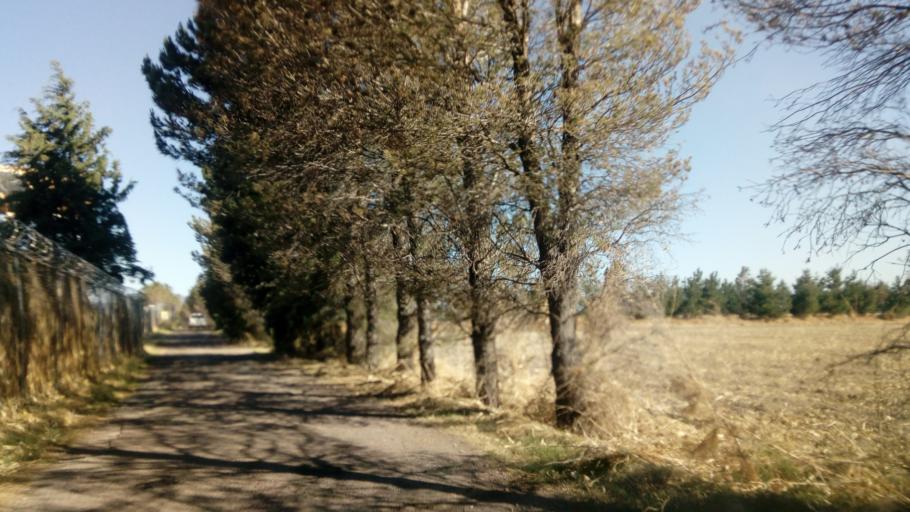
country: MX
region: Durango
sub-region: Durango
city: Jose Refugio Salcido
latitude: 24.0116
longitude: -104.5522
